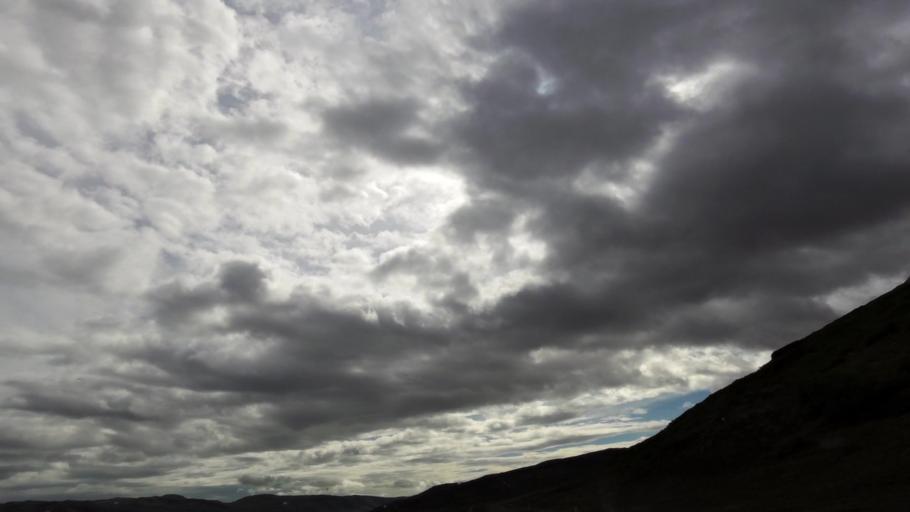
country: IS
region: West
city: Stykkisholmur
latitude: 65.5938
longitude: -22.1284
